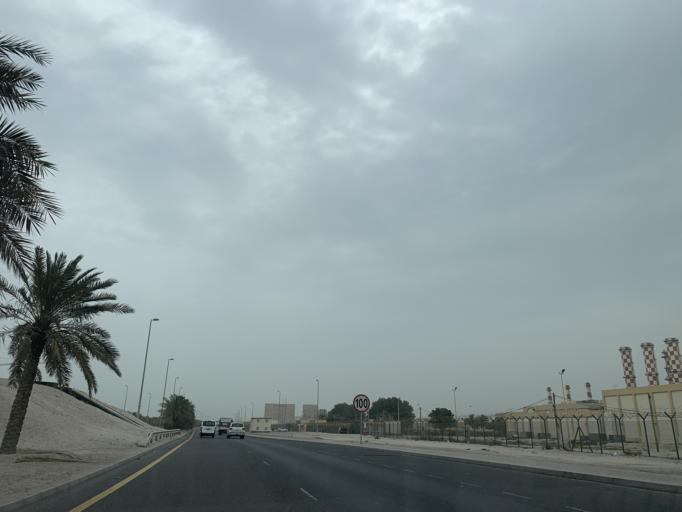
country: BH
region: Muharraq
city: Al Hadd
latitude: 26.2250
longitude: 50.6594
